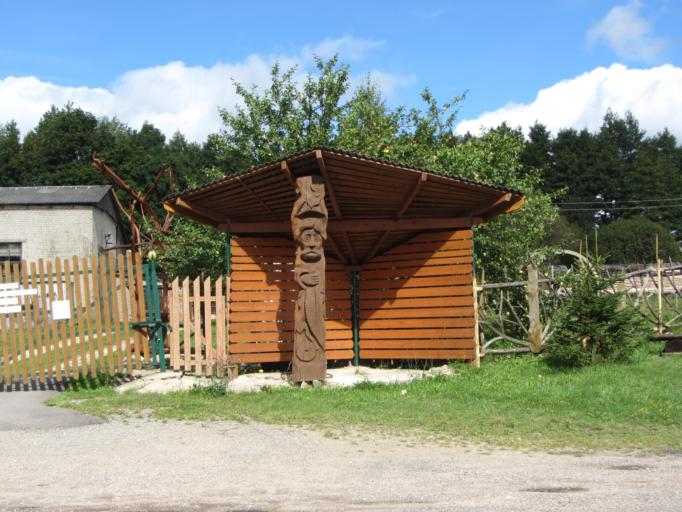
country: LT
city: Dukstas
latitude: 55.5465
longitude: 26.3354
